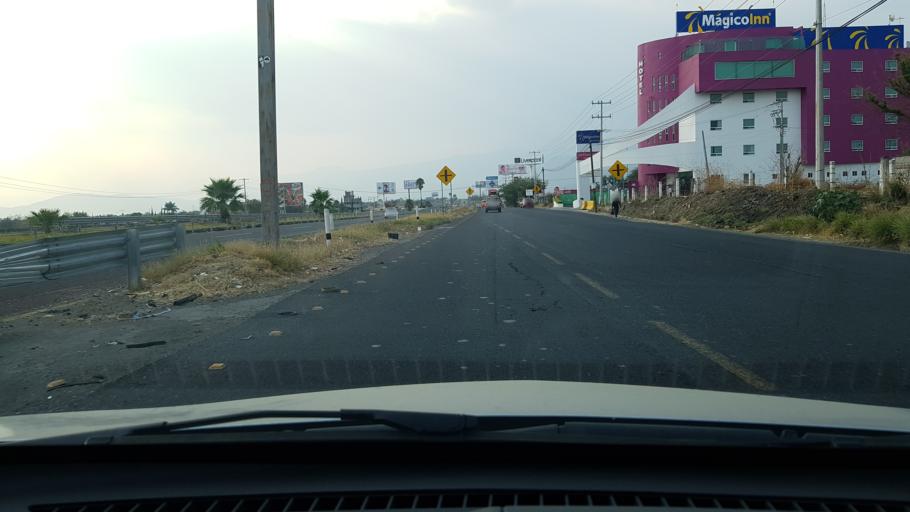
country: MX
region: Morelos
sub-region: Cuautla
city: Tierra Larga (Campo Nuevo)
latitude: 18.8645
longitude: -98.9490
